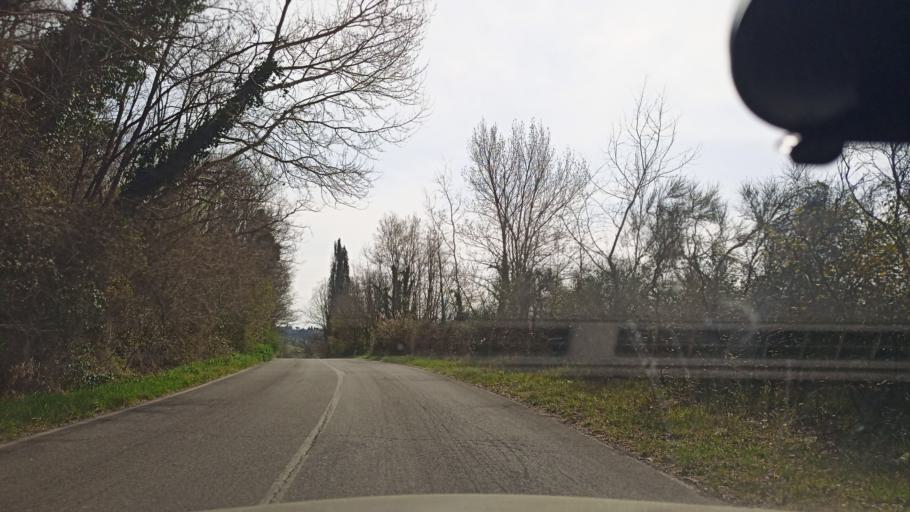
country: IT
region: Latium
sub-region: Provincia di Rieti
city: Cantalupo in Sabina
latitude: 42.3237
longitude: 12.6425
